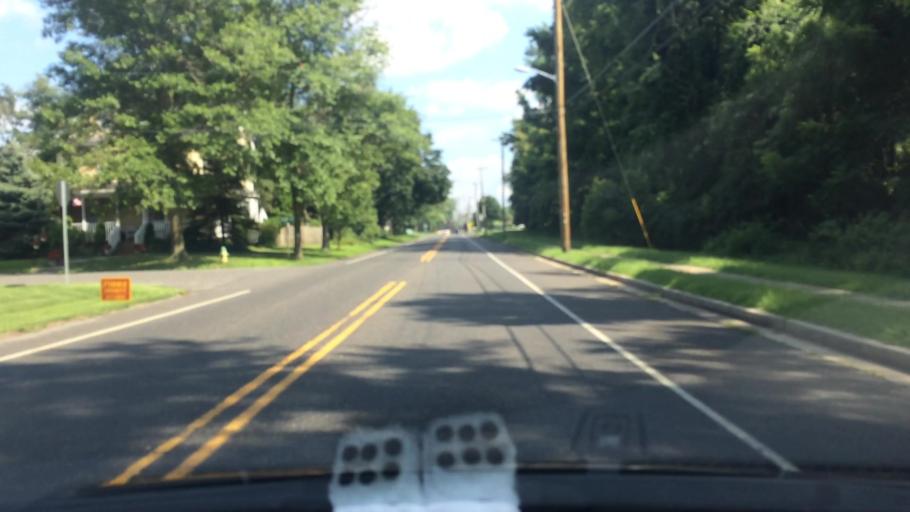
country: US
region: New Jersey
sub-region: Gloucester County
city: Turnersville
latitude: 39.7806
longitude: -75.0633
